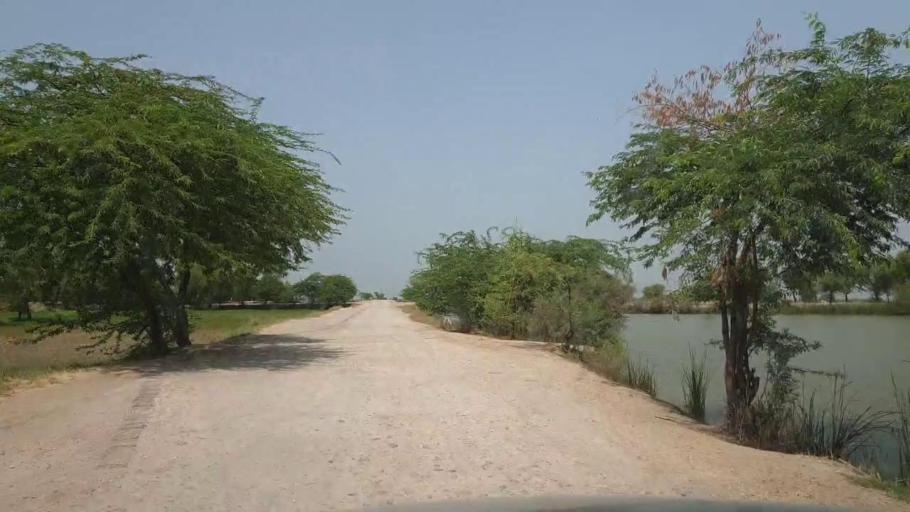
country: PK
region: Sindh
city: Garhi Yasin
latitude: 27.8775
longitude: 68.4455
